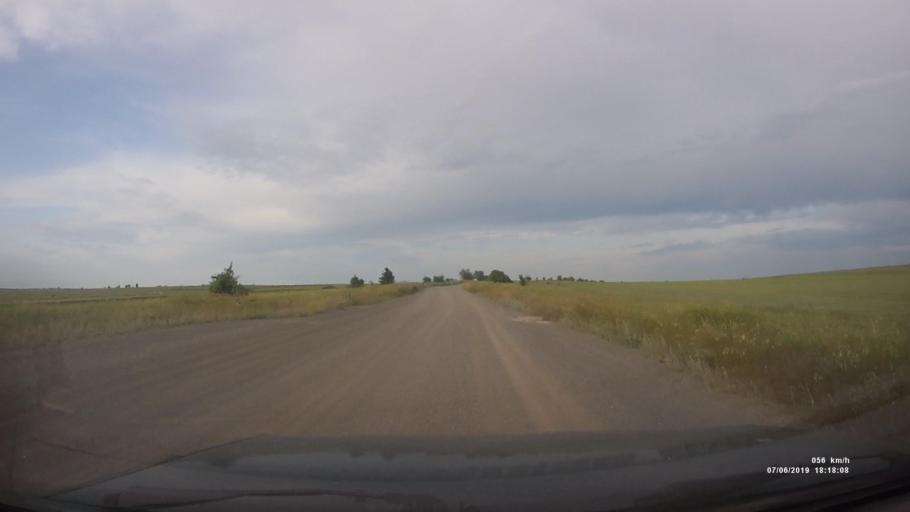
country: RU
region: Rostov
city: Staraya Stanitsa
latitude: 48.2548
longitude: 40.3580
